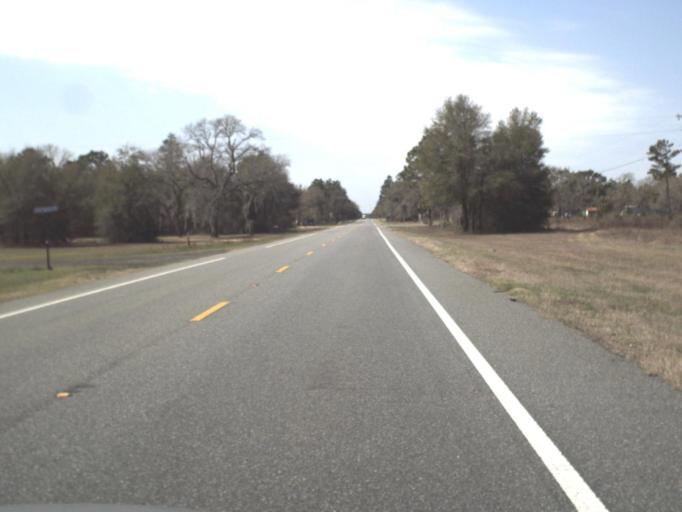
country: US
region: Florida
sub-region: Gadsden County
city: Gretna
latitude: 30.5270
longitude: -84.7930
